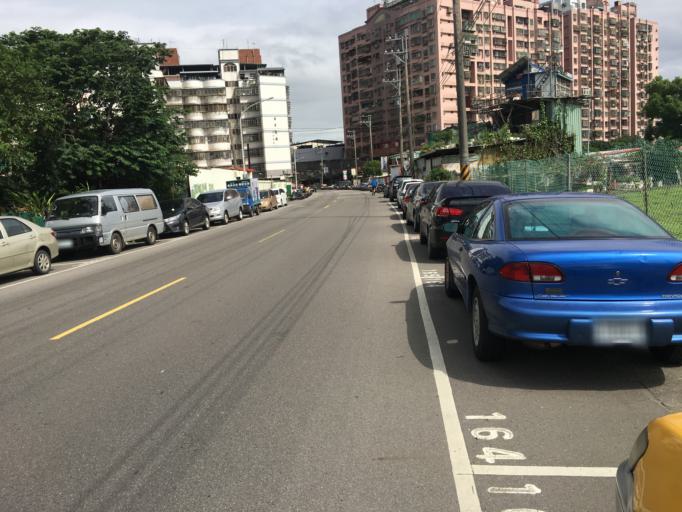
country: TW
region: Taipei
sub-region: Taipei
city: Banqiao
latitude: 24.9769
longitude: 121.4214
